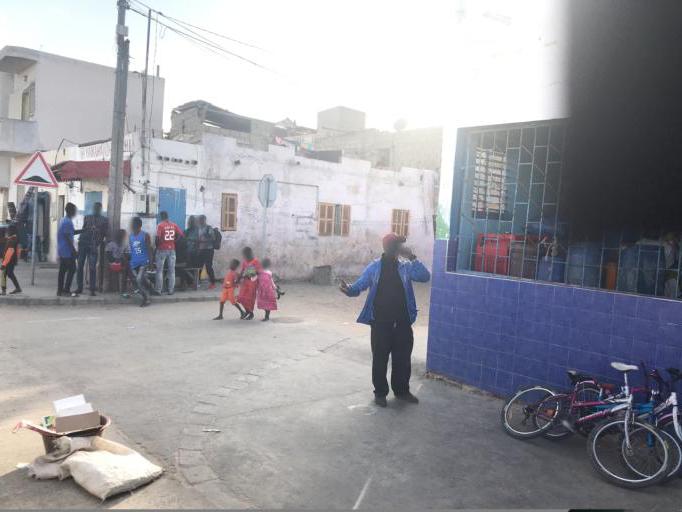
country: SN
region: Saint-Louis
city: Saint-Louis
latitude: 16.0243
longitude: -16.5073
